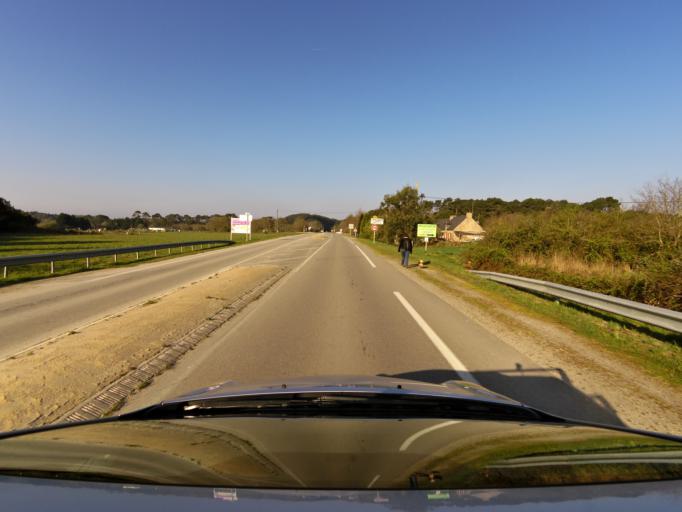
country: FR
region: Brittany
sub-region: Departement du Morbihan
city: Ploemeur
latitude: 47.7385
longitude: -3.4552
